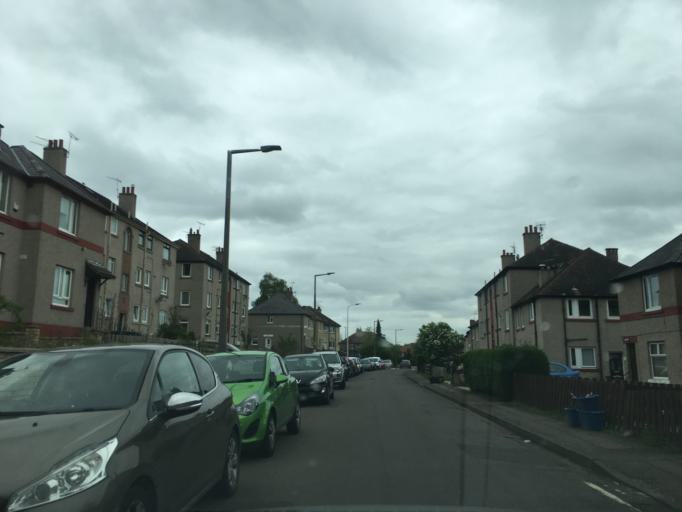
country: GB
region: Scotland
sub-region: Edinburgh
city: Colinton
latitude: 55.9210
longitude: -3.2805
